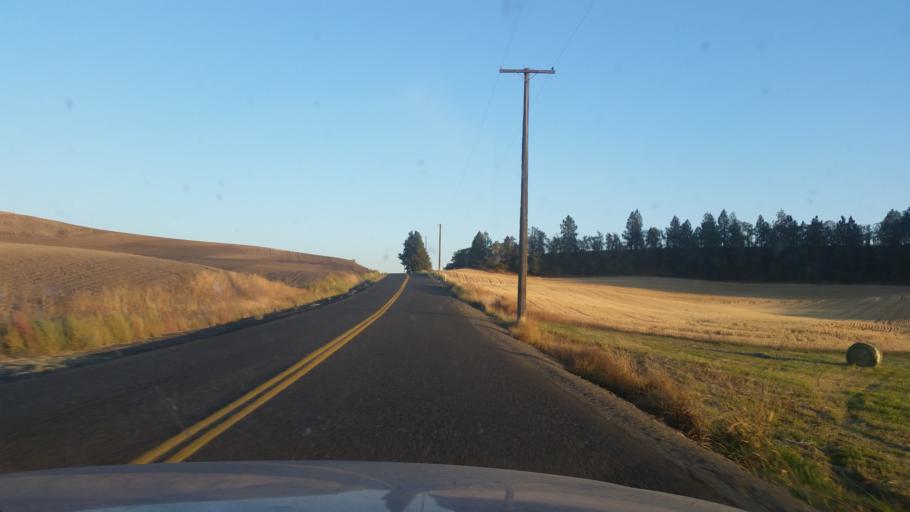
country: US
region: Washington
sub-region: Spokane County
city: Cheney
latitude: 47.5189
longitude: -117.5971
